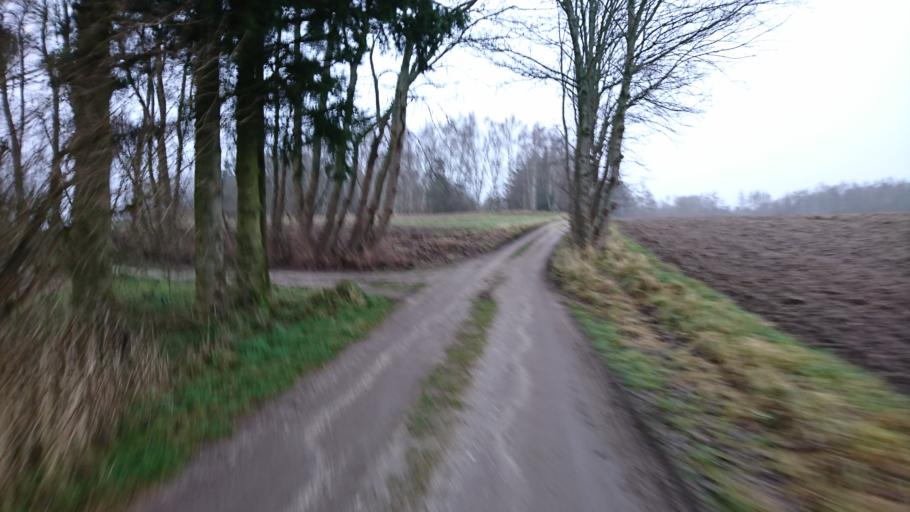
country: DK
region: Capital Region
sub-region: Ballerup Kommune
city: Ballerup
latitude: 55.7432
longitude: 12.3455
